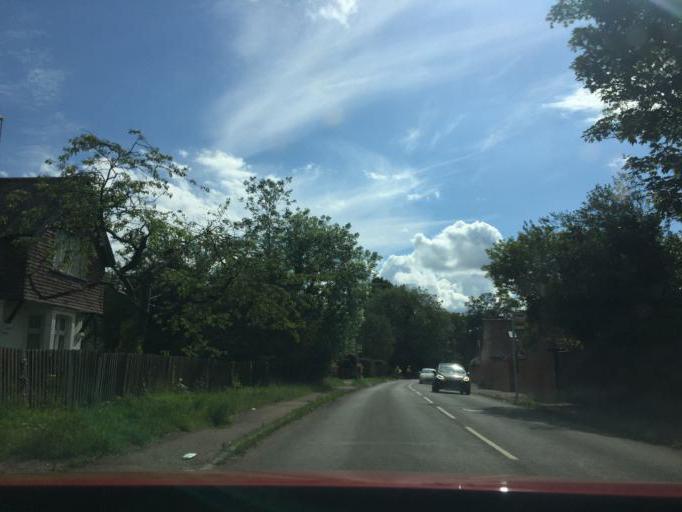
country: GB
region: England
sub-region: Hertfordshire
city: Knebworth
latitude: 51.8693
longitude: -0.2126
